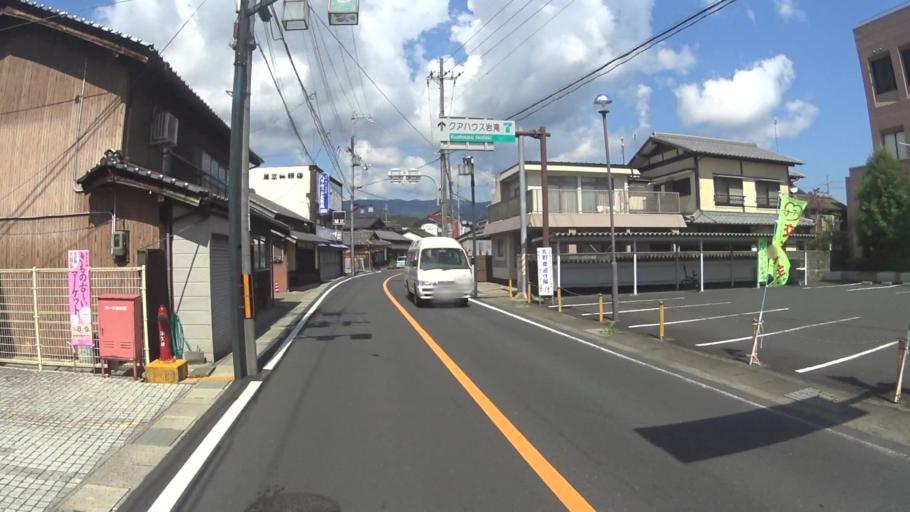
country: JP
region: Kyoto
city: Miyazu
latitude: 35.5654
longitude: 135.1524
